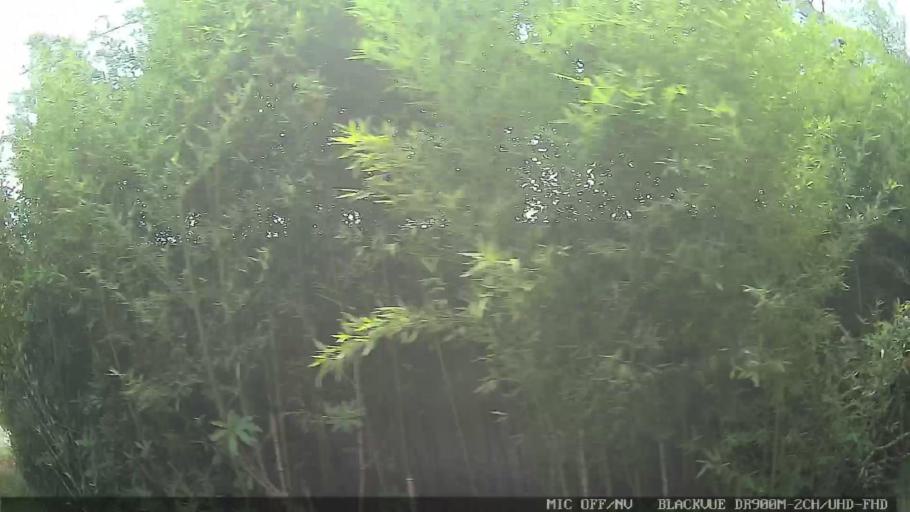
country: BR
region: Sao Paulo
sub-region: Aruja
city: Aruja
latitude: -23.4150
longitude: -46.3372
